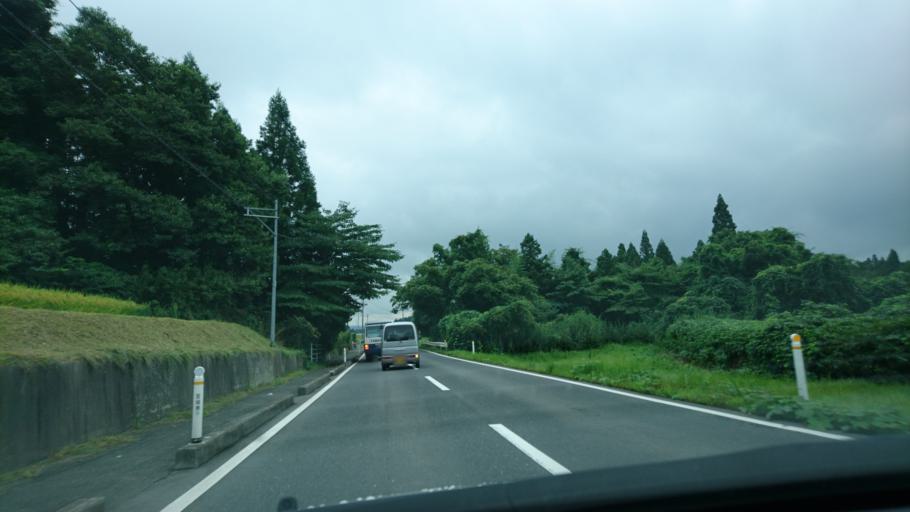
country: JP
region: Iwate
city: Ichinoseki
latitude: 38.8059
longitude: 140.9320
